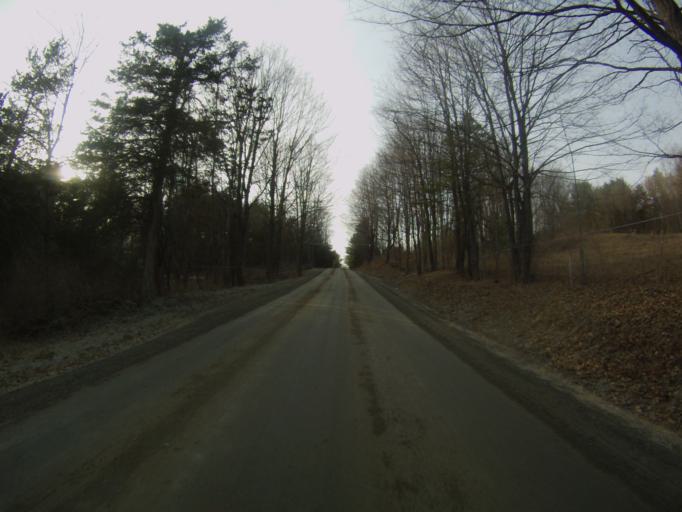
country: US
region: Vermont
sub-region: Addison County
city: Middlebury (village)
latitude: 44.0372
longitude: -73.2740
